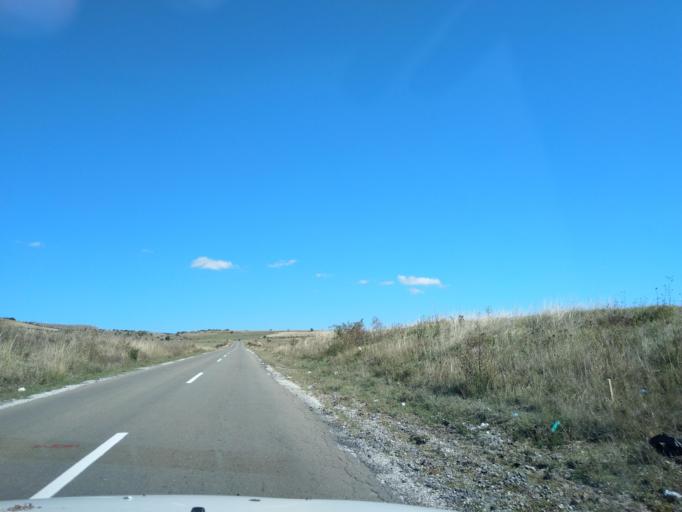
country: RS
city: Sokolovica
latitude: 43.2751
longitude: 20.2098
